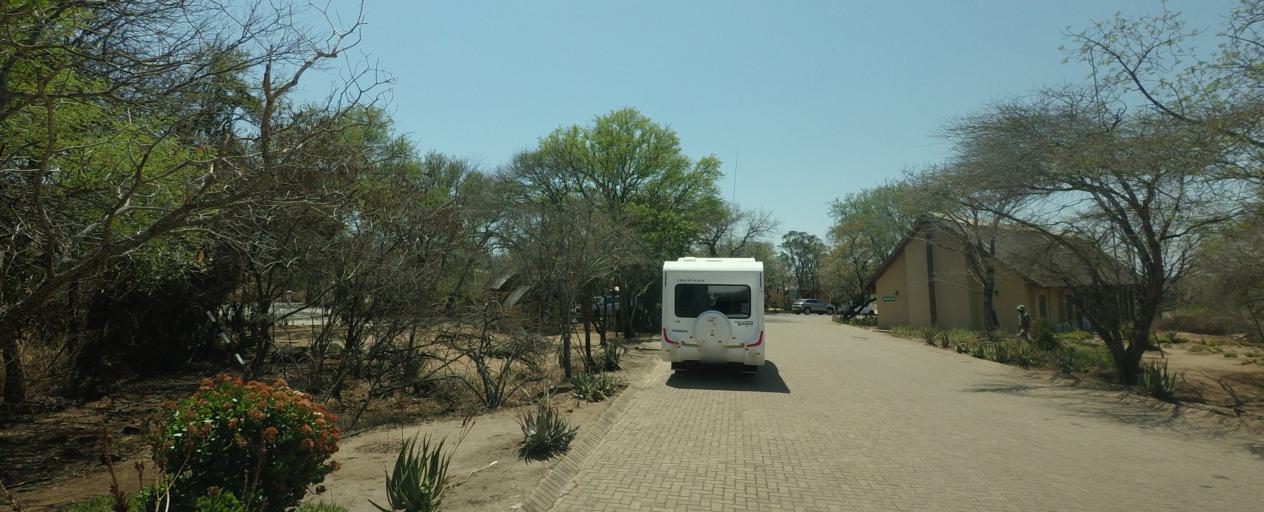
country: ZA
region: Limpopo
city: Thulamahashi
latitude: -24.4762
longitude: 31.3905
